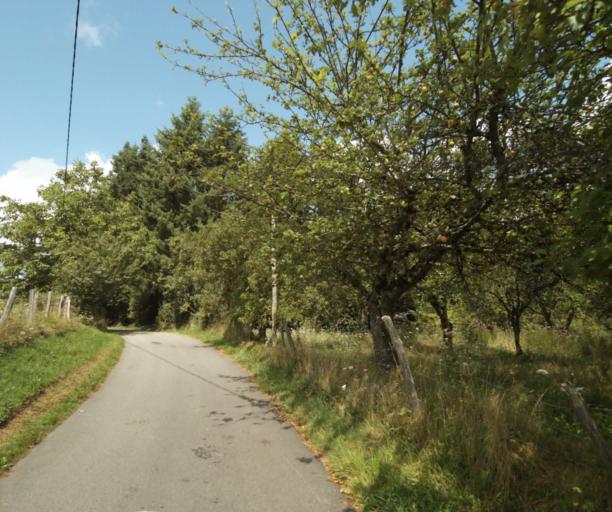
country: FR
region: Limousin
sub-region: Departement de la Correze
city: Sainte-Fortunade
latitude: 45.1944
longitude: 1.8280
